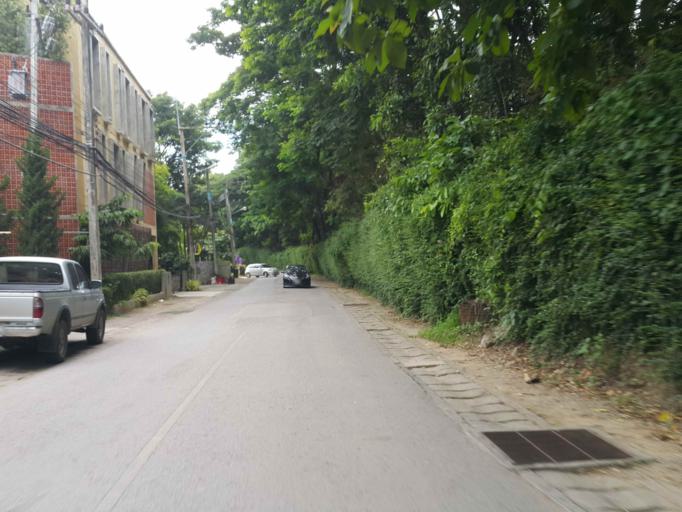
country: TH
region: Chiang Mai
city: San Sai
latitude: 18.9137
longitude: 98.9300
